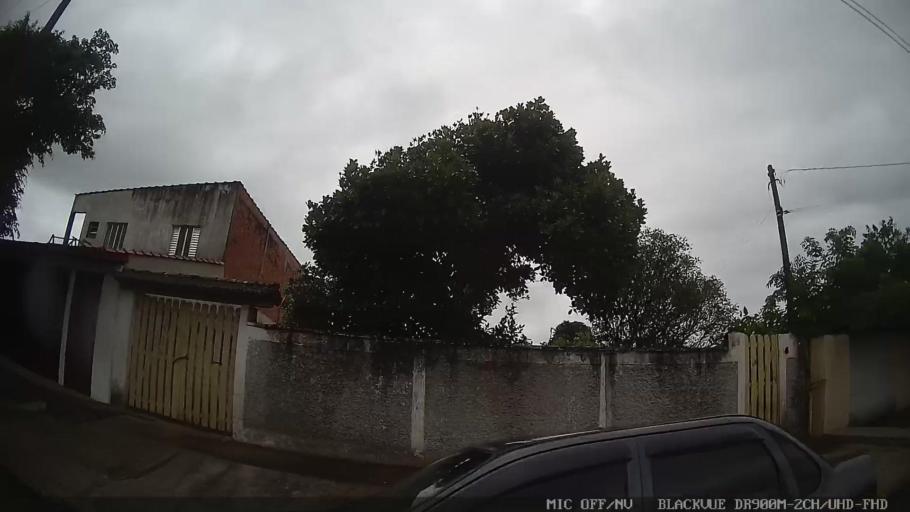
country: BR
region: Sao Paulo
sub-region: Itanhaem
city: Itanhaem
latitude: -24.1802
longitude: -46.8209
